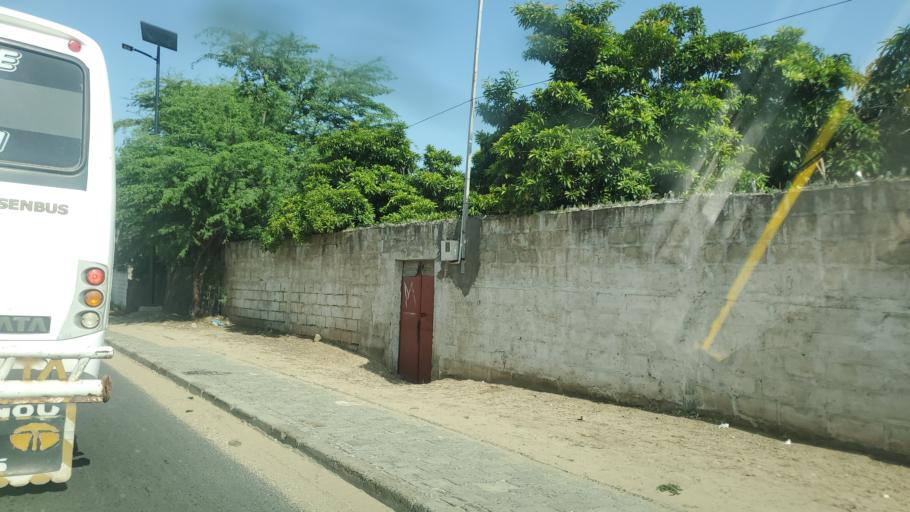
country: SN
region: Saint-Louis
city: Saint-Louis
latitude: 16.0370
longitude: -16.4609
